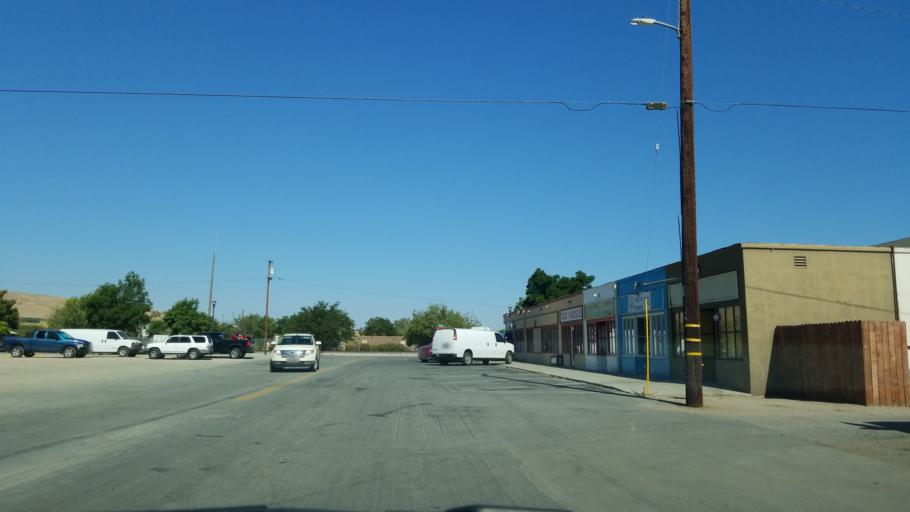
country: US
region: California
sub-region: San Luis Obispo County
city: San Miguel
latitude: 35.7516
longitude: -120.6972
